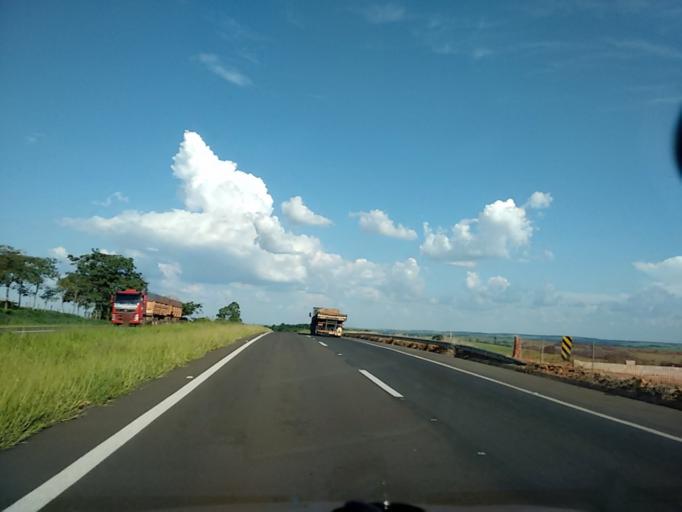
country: BR
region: Sao Paulo
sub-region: Garca
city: Garca
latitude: -22.2647
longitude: -49.5182
